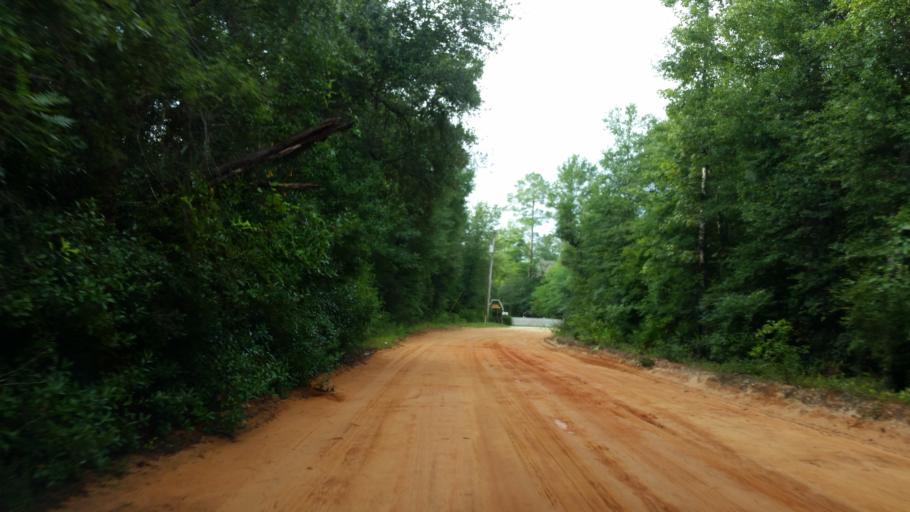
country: US
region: Florida
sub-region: Okaloosa County
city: Crestview
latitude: 30.6711
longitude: -86.7567
